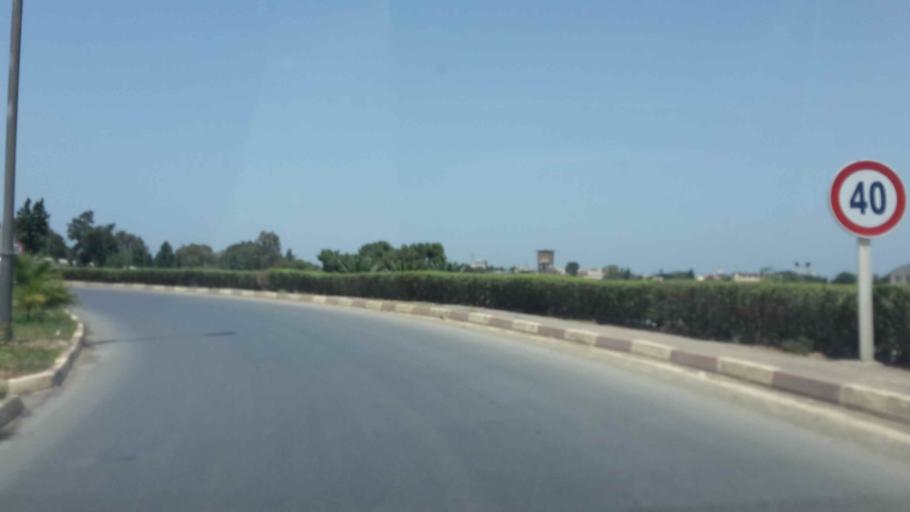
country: DZ
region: Alger
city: Dar el Beida
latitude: 36.7035
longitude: 3.2079
